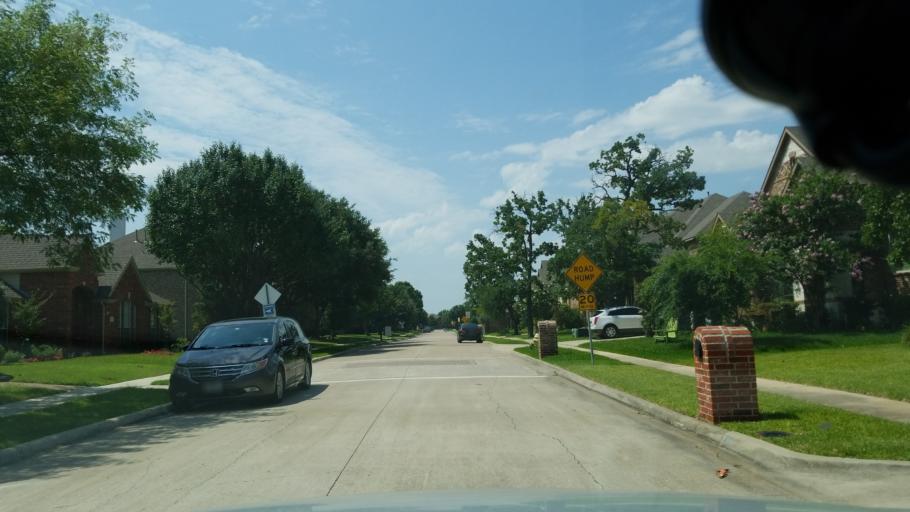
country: US
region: Texas
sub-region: Dallas County
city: Coppell
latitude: 32.9690
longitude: -96.9873
